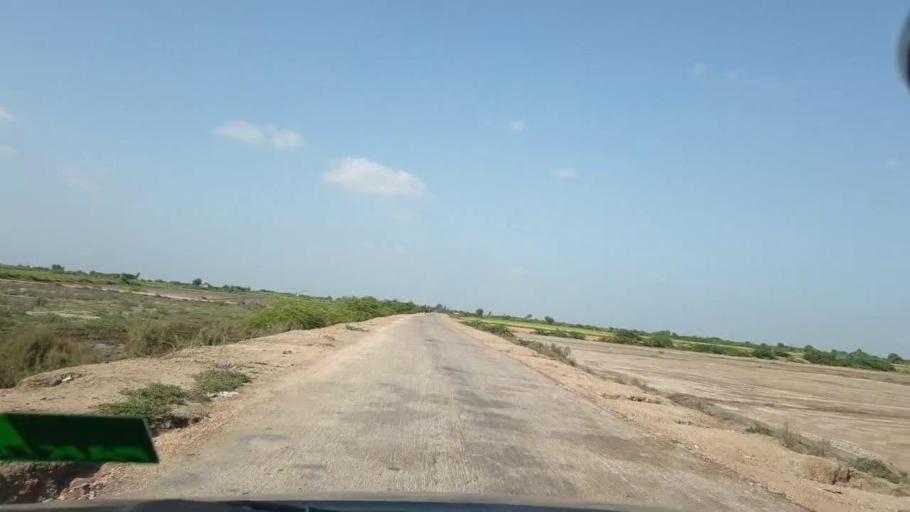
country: PK
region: Sindh
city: Tando Bago
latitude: 24.6986
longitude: 69.1904
